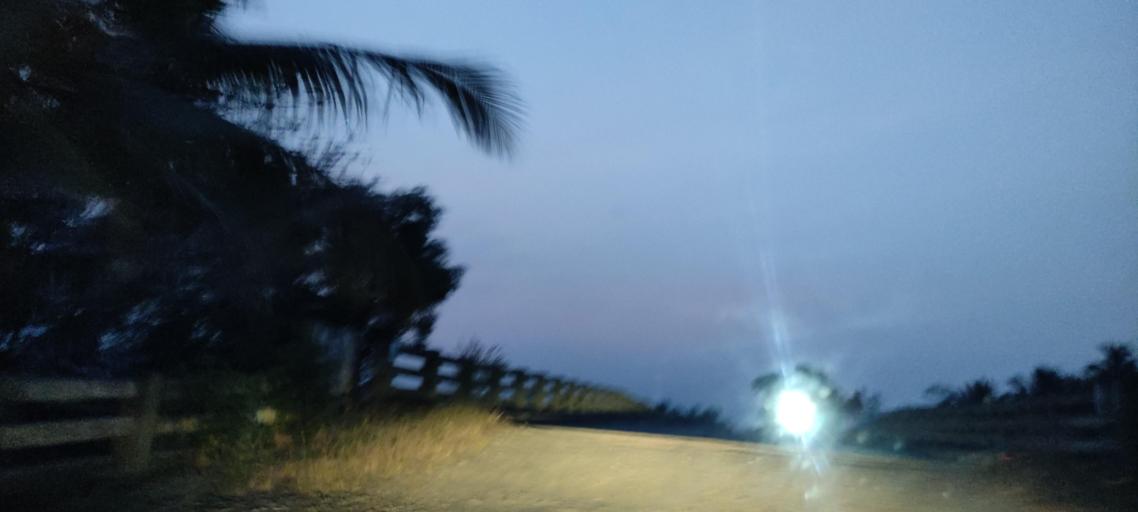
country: IN
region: Kerala
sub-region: Alappuzha
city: Mavelikara
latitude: 9.3202
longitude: 76.4353
